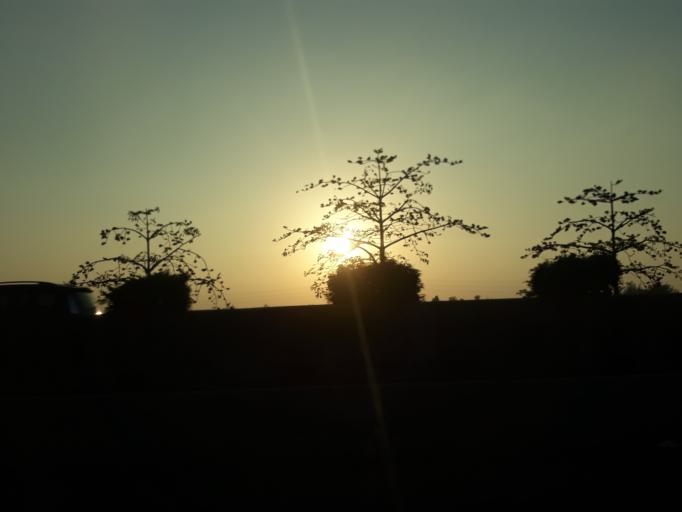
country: TW
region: Taiwan
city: Fengshan
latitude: 22.7694
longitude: 120.3275
